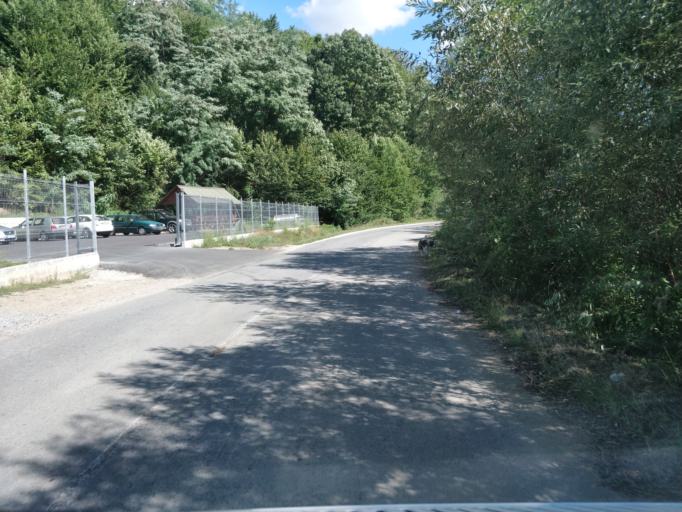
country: RO
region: Cluj
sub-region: Comuna Sacueu
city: Sacuieu
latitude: 46.8639
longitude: 22.8699
